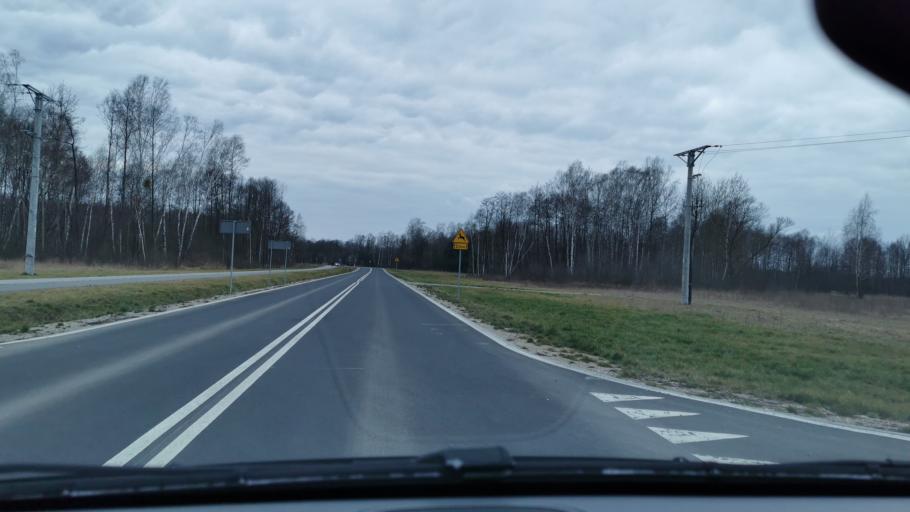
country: PL
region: Masovian Voivodeship
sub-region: Powiat zyrardowski
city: Zyrardow
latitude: 52.0106
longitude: 20.4710
